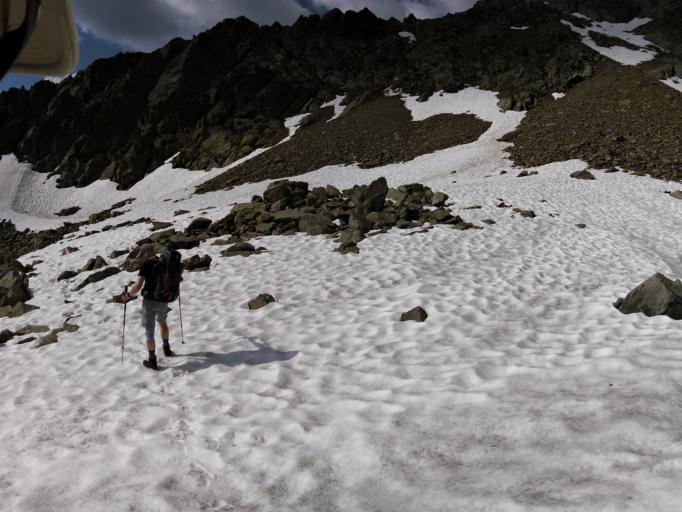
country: AT
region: Tyrol
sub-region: Politischer Bezirk Innsbruck Land
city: Gschnitz
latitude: 47.0384
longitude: 11.3031
